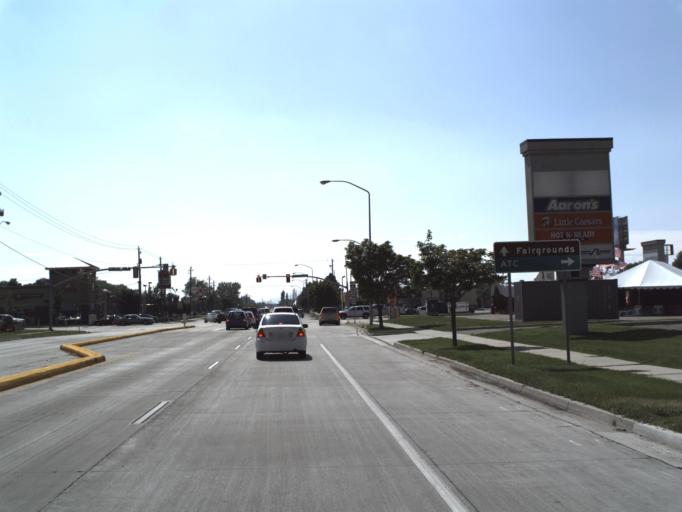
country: US
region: Utah
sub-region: Weber County
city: Ogden
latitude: 41.2443
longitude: -111.9652
